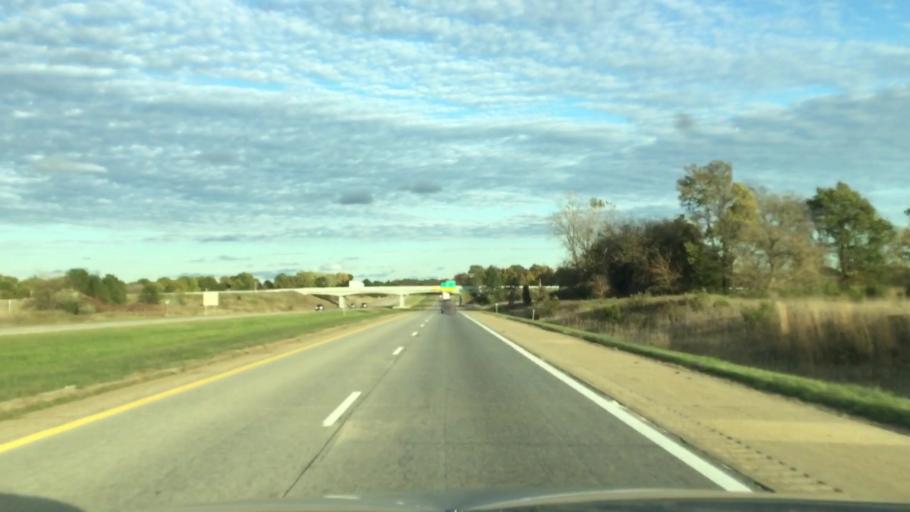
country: US
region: Michigan
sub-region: Calhoun County
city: Albion
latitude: 42.2631
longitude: -84.7125
